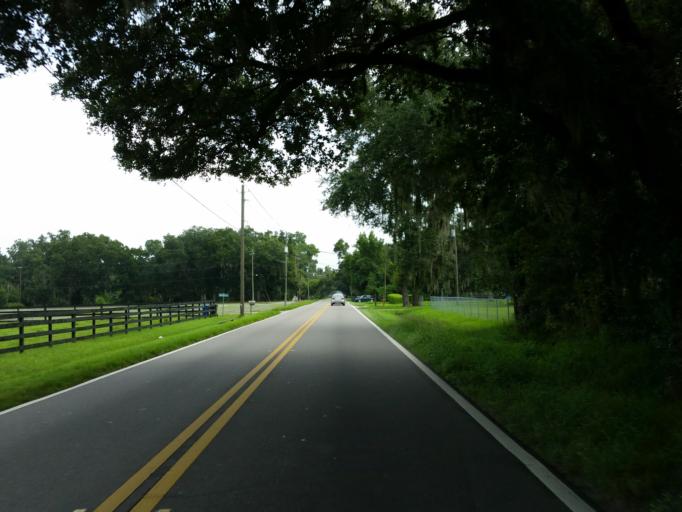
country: US
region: Florida
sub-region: Hillsborough County
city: Dover
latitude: 28.0050
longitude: -82.2445
